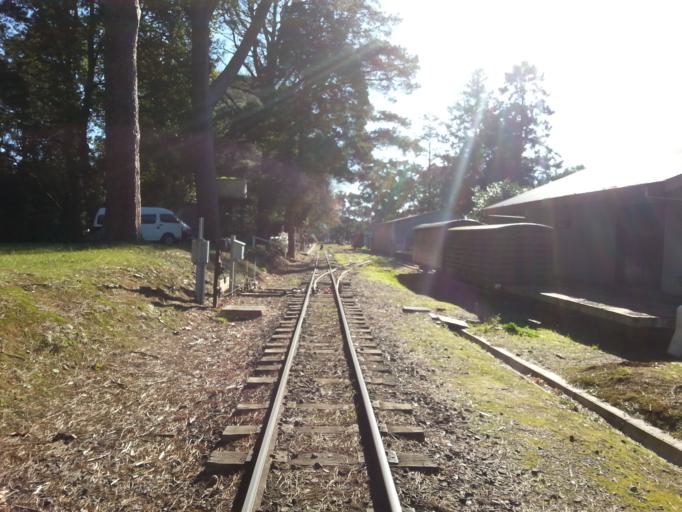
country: AU
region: Victoria
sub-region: Cardinia
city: Emerald
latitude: -37.9341
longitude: 145.4402
